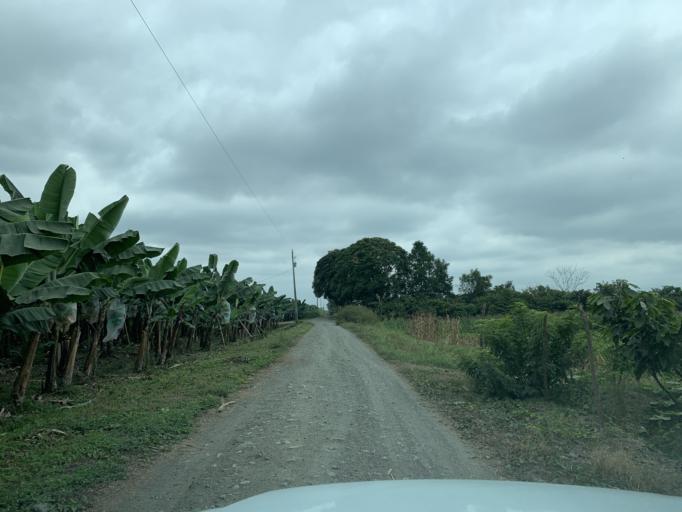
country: EC
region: Guayas
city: Coronel Marcelino Mariduena
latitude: -2.3422
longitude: -79.4579
